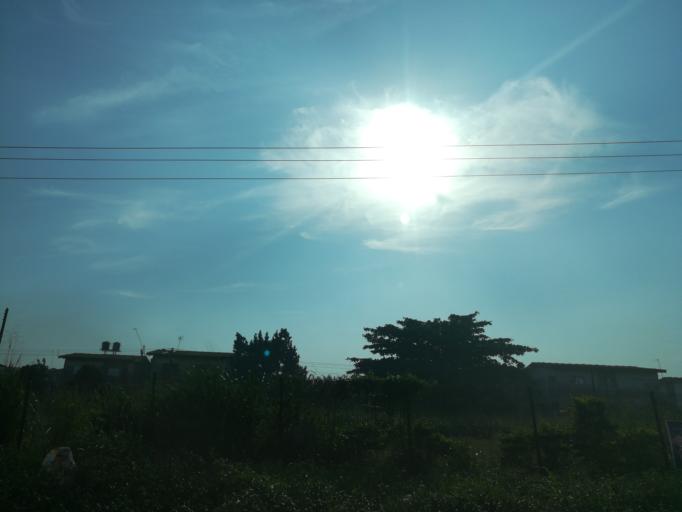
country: NG
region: Rivers
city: Port Harcourt
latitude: 4.8231
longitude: 7.0244
